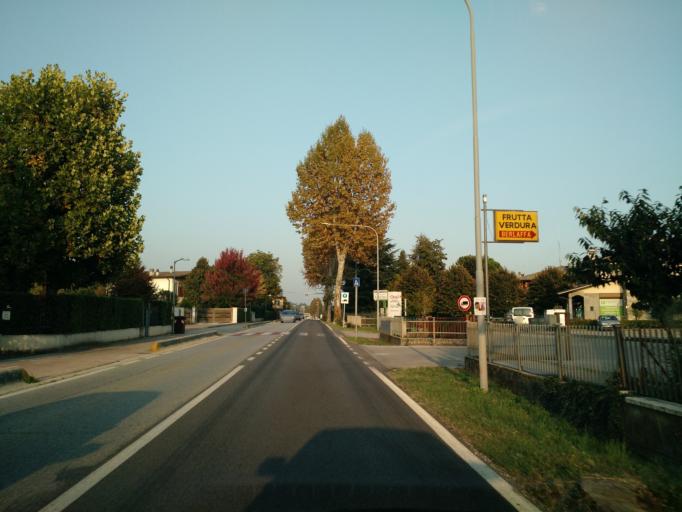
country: IT
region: Veneto
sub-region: Provincia di Vicenza
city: Sarcedo
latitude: 45.7024
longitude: 11.5358
